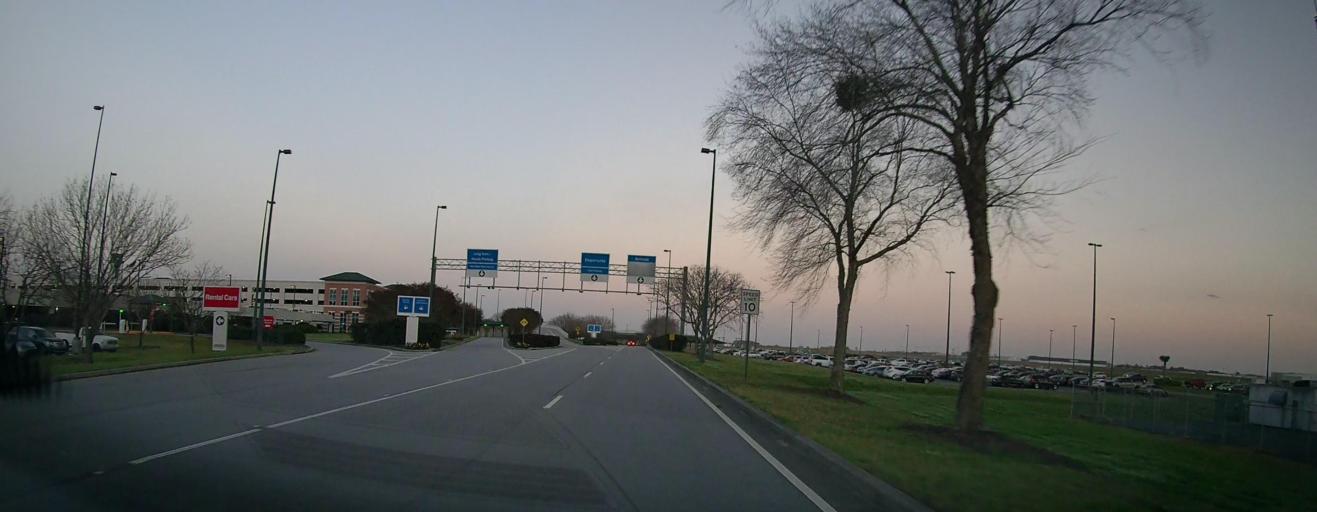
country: US
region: Georgia
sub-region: Chatham County
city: Pooler
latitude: 32.1338
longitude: -81.2134
